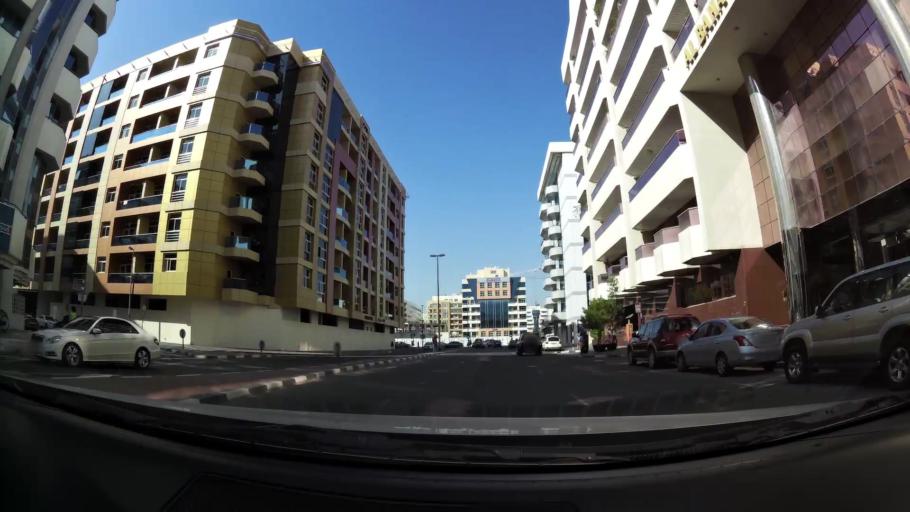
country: AE
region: Ash Shariqah
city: Sharjah
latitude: 25.2530
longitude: 55.2986
